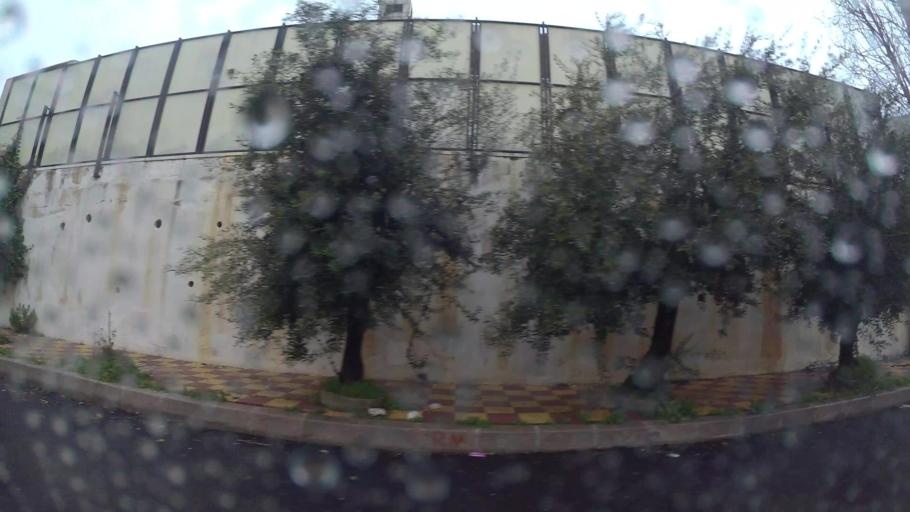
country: JO
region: Amman
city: Al Jubayhah
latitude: 32.0022
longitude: 35.8281
